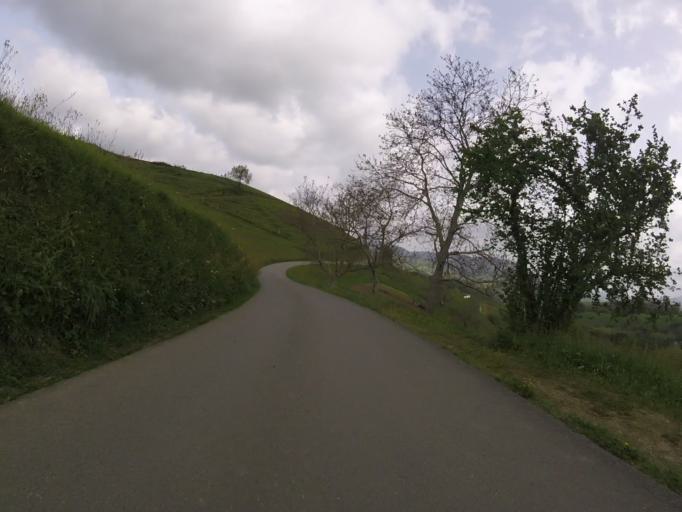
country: ES
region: Basque Country
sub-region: Provincia de Guipuzcoa
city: Irura
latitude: 43.1781
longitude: -2.0826
